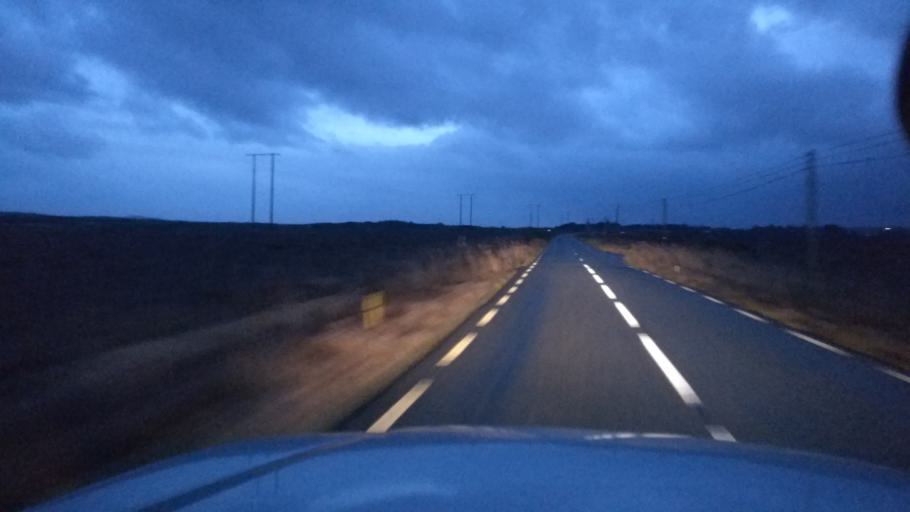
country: IE
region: Connaught
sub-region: County Galway
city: Oughterard
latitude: 53.4015
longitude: -9.5441
